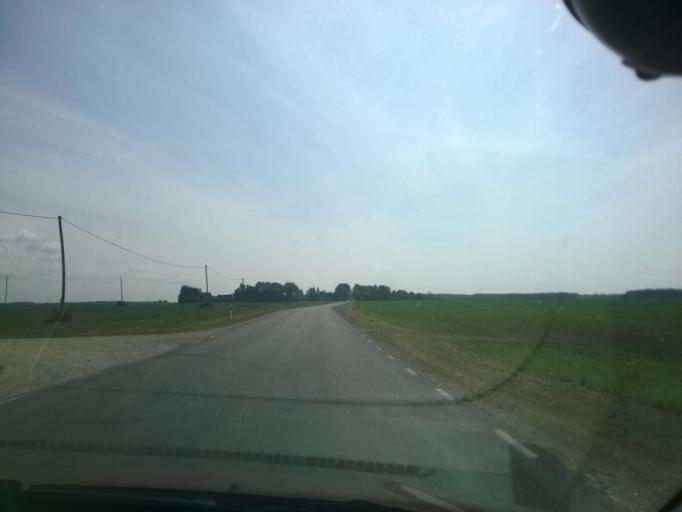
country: EE
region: Tartu
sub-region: Puhja vald
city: Puhja
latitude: 58.2780
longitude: 26.1755
